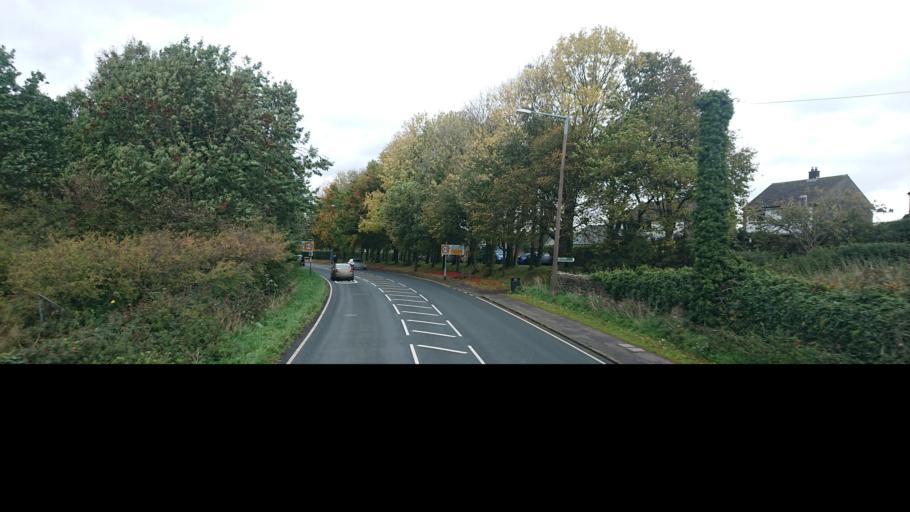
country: GB
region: England
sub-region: Lancashire
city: Lancaster
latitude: 54.0236
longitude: -2.7950
